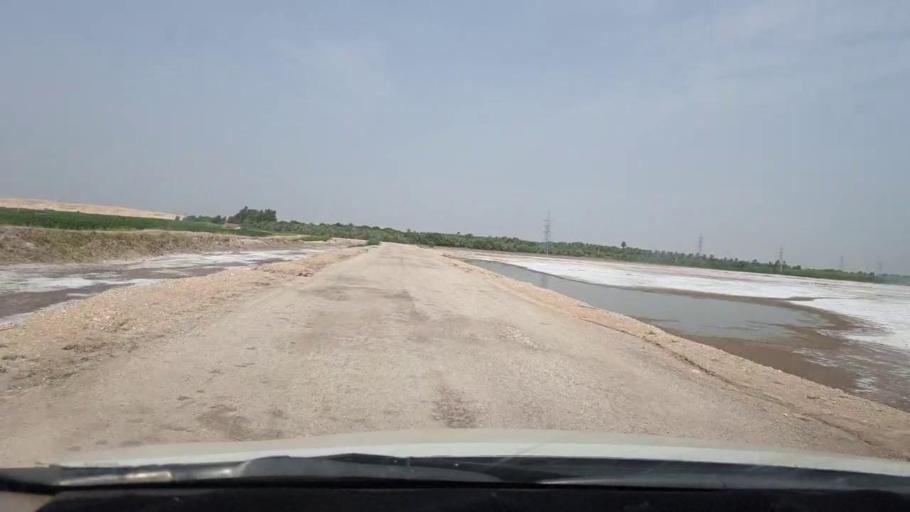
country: PK
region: Sindh
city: Rohri
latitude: 27.5958
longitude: 68.9876
